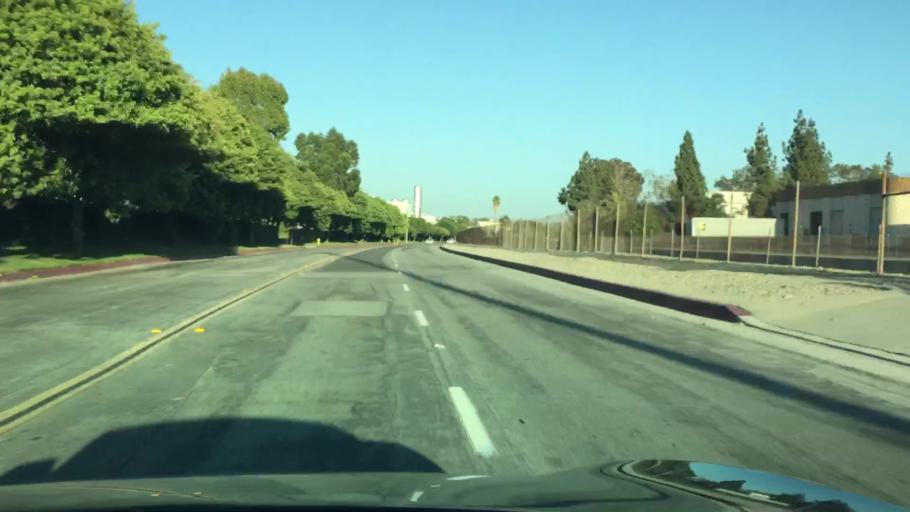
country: US
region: California
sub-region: Los Angeles County
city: South San Jose Hills
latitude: 34.0051
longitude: -117.9104
